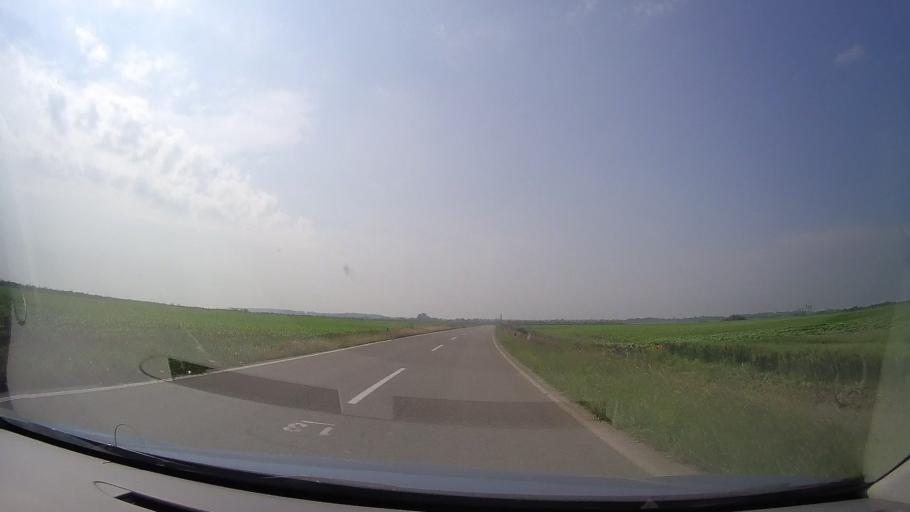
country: RS
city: Jasa Tomic
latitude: 45.4660
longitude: 20.8518
